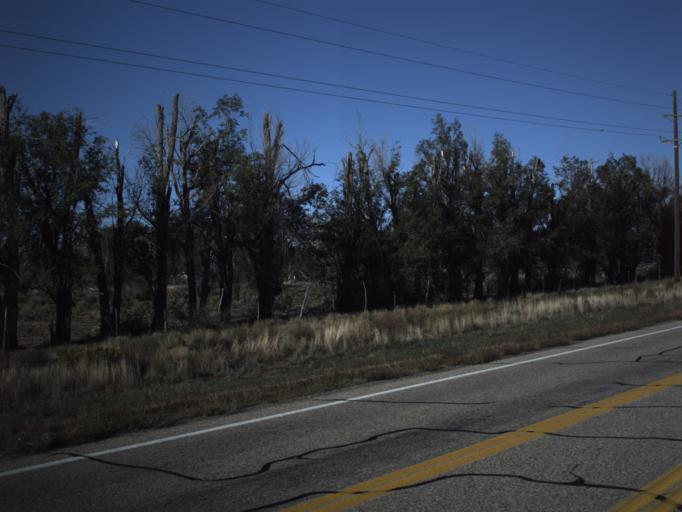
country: US
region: Utah
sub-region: Washington County
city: Enterprise
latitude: 37.7104
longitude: -113.6587
